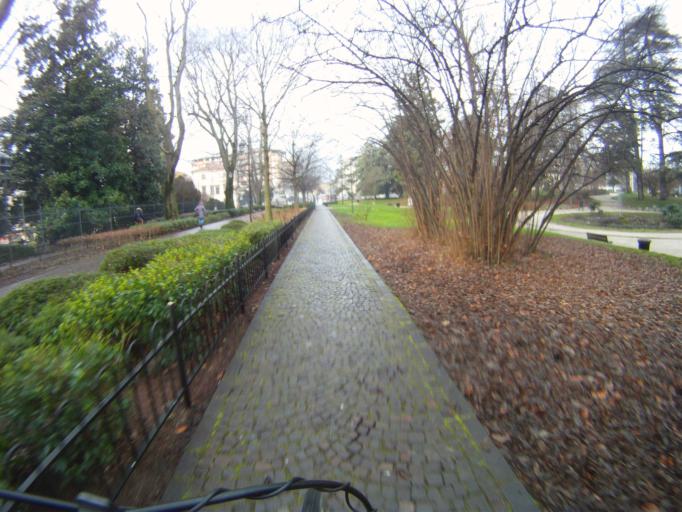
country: IT
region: Veneto
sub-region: Provincia di Padova
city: Padova
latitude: 45.4121
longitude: 11.8800
